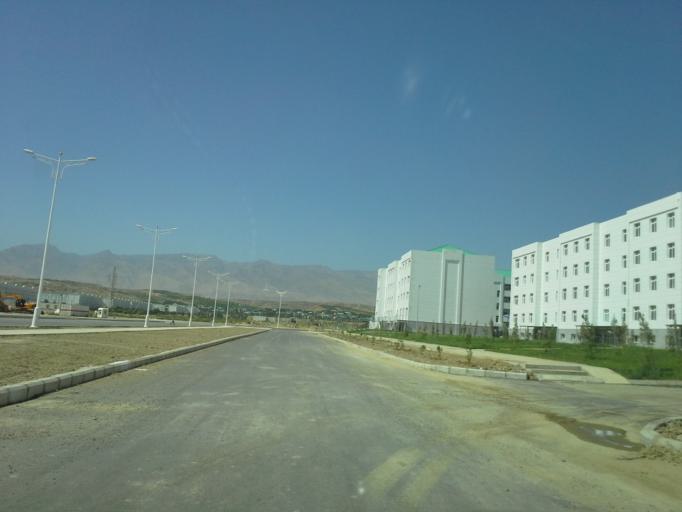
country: TM
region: Ahal
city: Ashgabat
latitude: 37.9725
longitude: 58.3296
